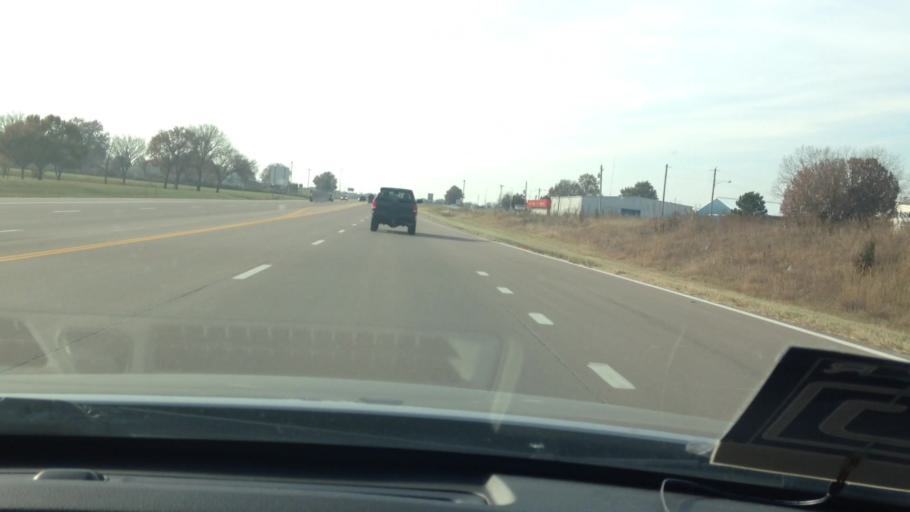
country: US
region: Missouri
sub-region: Henry County
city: Clinton
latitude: 38.3881
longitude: -93.7615
